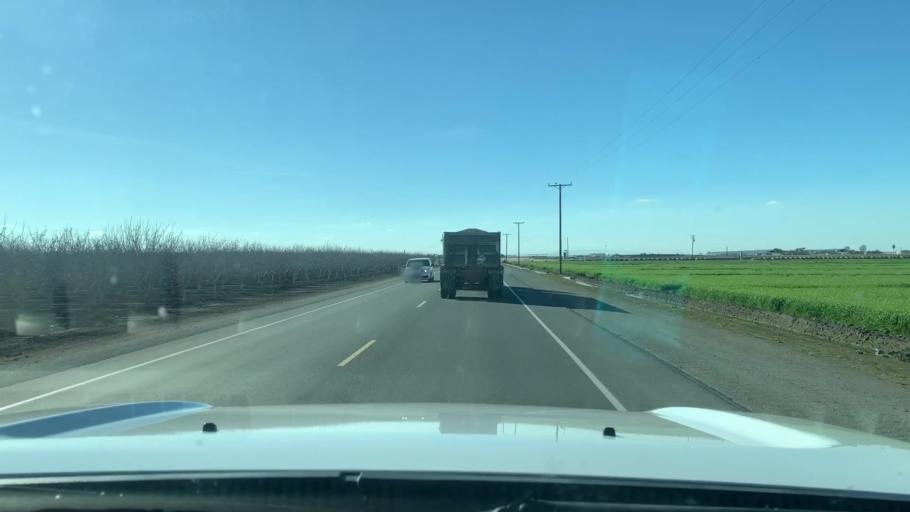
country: US
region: California
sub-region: Kings County
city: Corcoran
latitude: 36.2111
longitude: -119.5165
